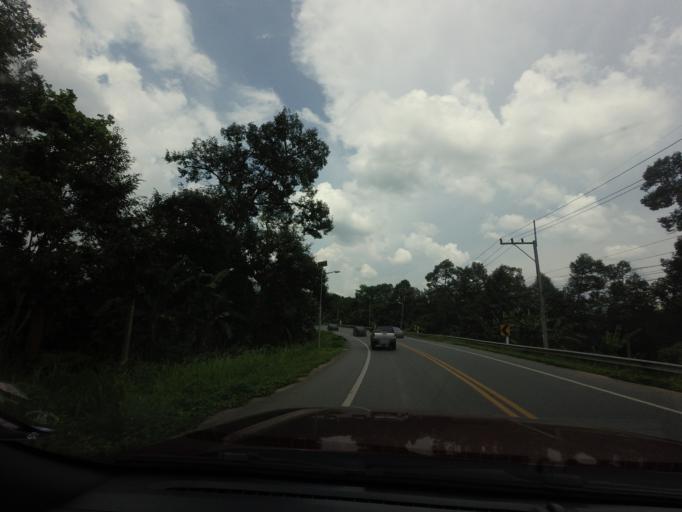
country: TH
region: Yala
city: Ban Nang Sata
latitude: 6.2640
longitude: 101.2749
